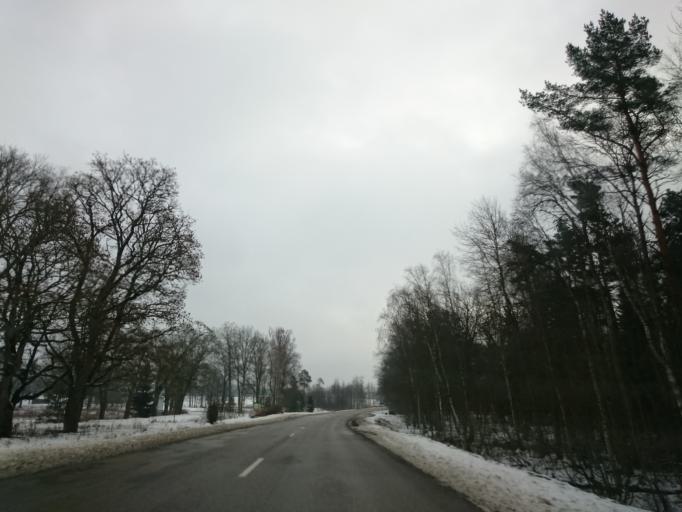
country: LV
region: Pargaujas
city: Stalbe
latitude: 57.3530
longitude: 25.0896
